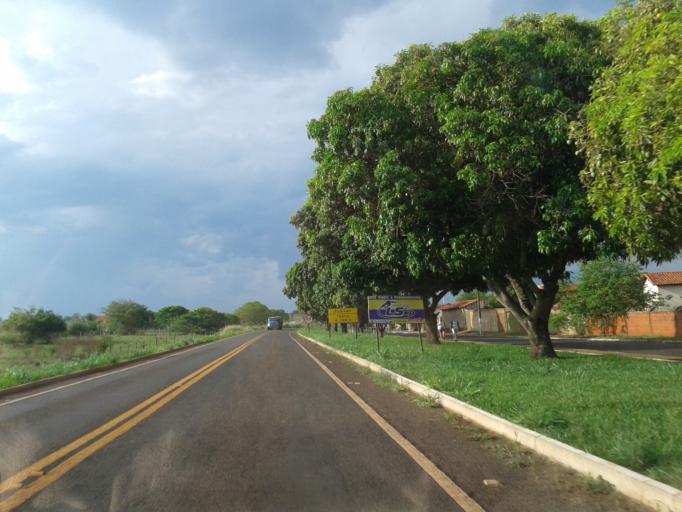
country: BR
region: Goias
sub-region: Quirinopolis
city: Quirinopolis
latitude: -18.9086
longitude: -50.6611
